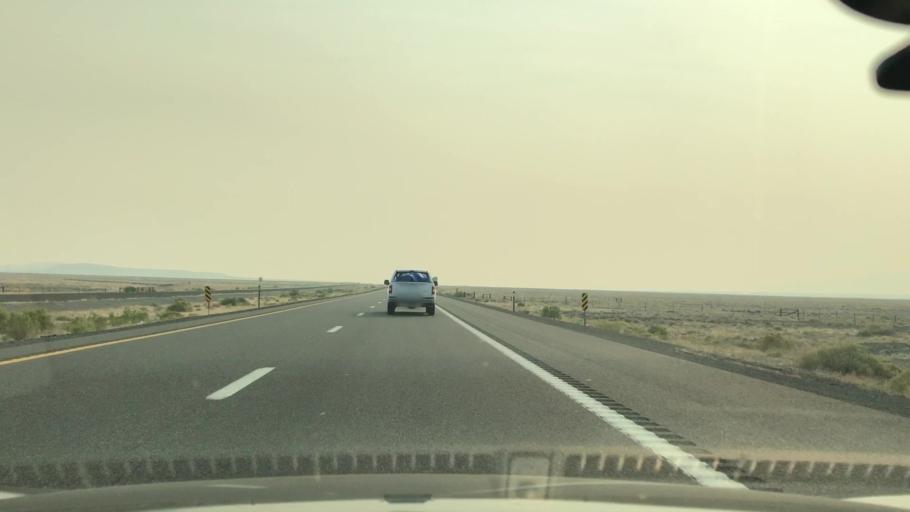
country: US
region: Nevada
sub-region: Pershing County
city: Lovelock
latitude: 39.9331
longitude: -118.7719
